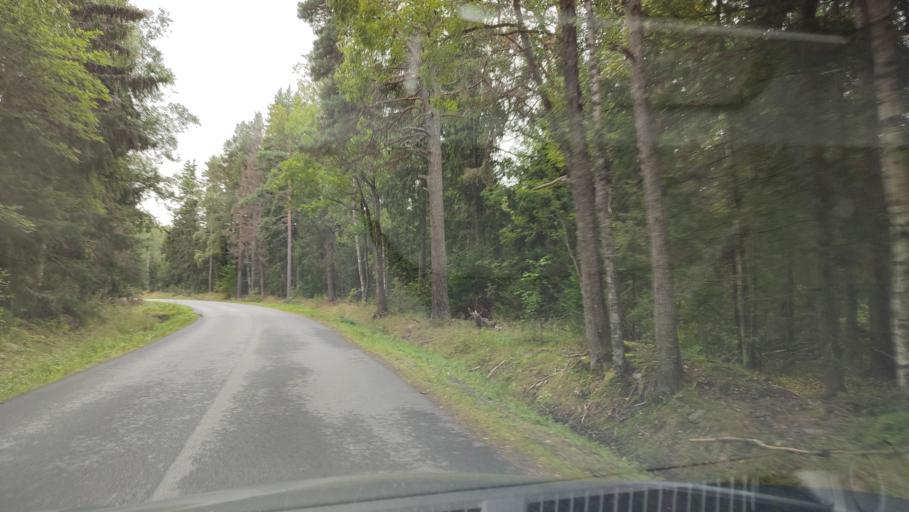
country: FI
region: Ostrobothnia
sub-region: Sydosterbotten
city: Kristinestad
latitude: 62.2576
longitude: 21.3572
